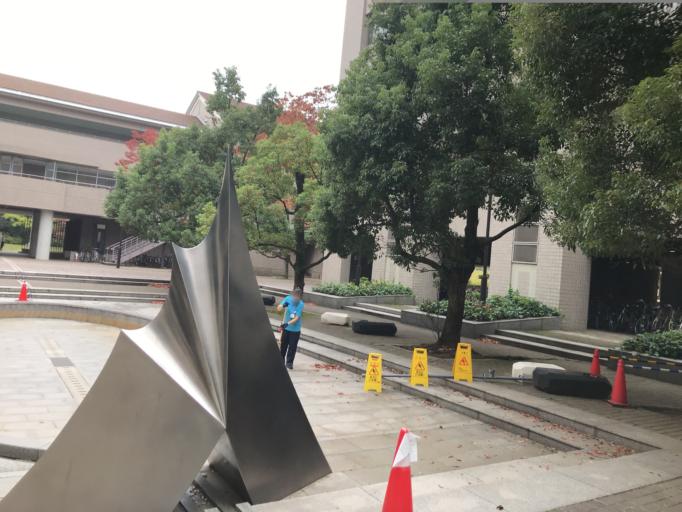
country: JP
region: Tokyo
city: Hino
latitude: 35.6201
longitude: 139.3820
